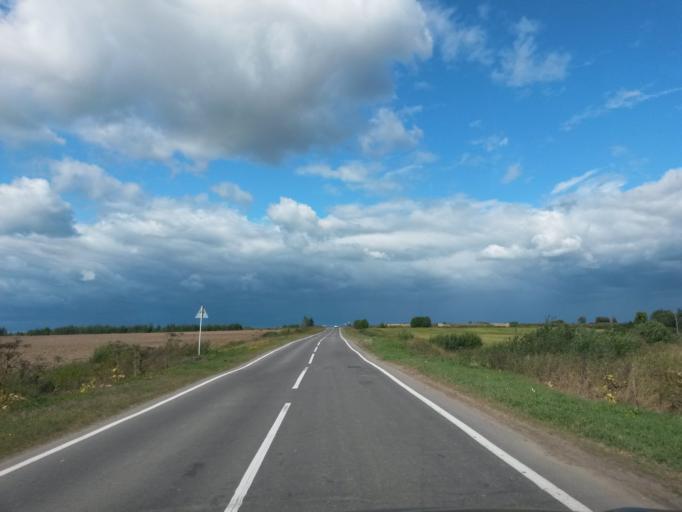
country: RU
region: Jaroslavl
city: Yaroslavl
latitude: 57.7480
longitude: 39.8808
